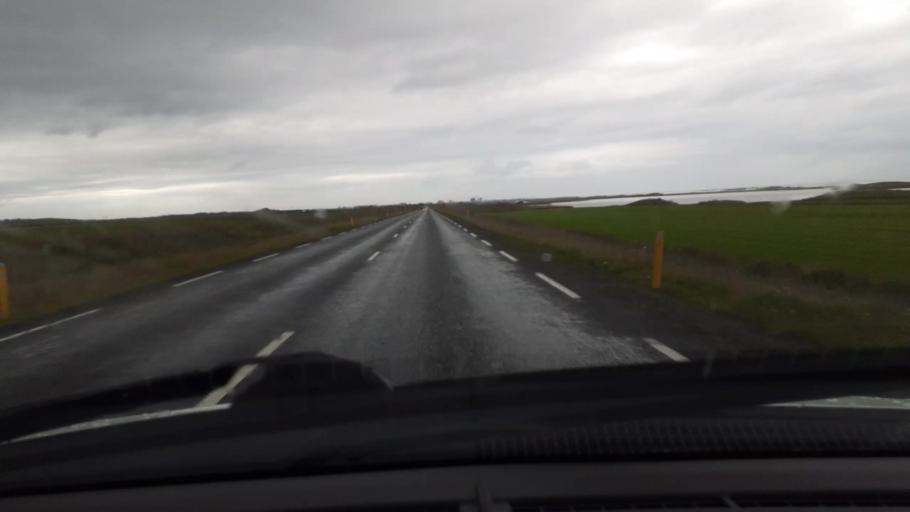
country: IS
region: West
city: Akranes
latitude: 64.3506
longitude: -21.9970
